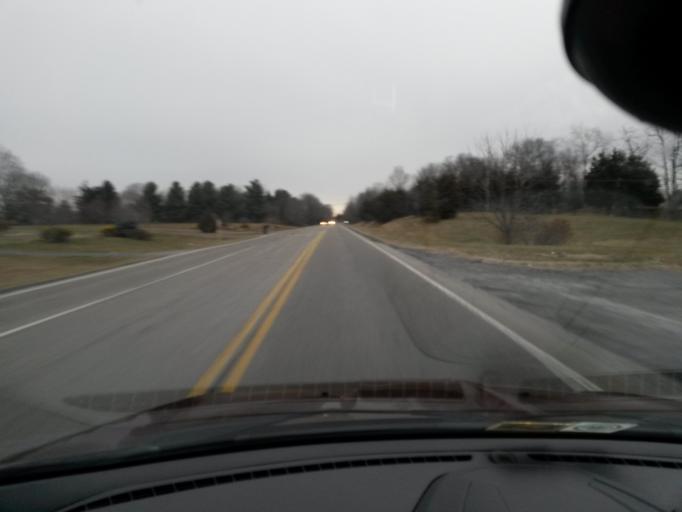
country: US
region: Virginia
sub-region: Augusta County
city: Stuarts Draft
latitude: 37.9501
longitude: -79.1839
